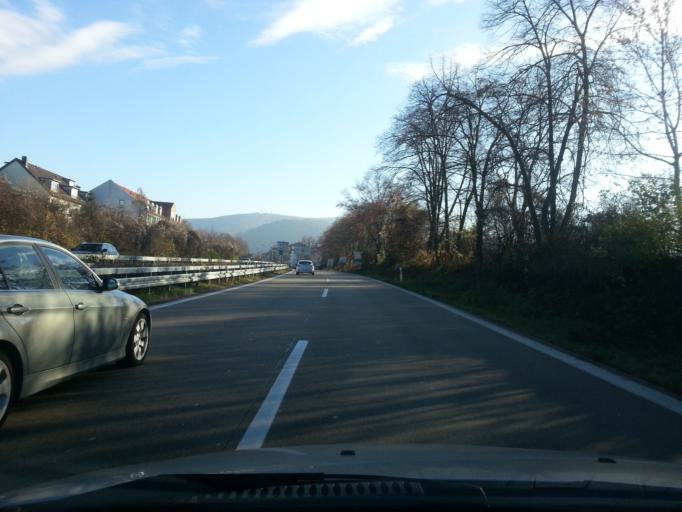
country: DE
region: Baden-Wuerttemberg
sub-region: Karlsruhe Region
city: Heidelberg
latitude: 49.4084
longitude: 8.6648
